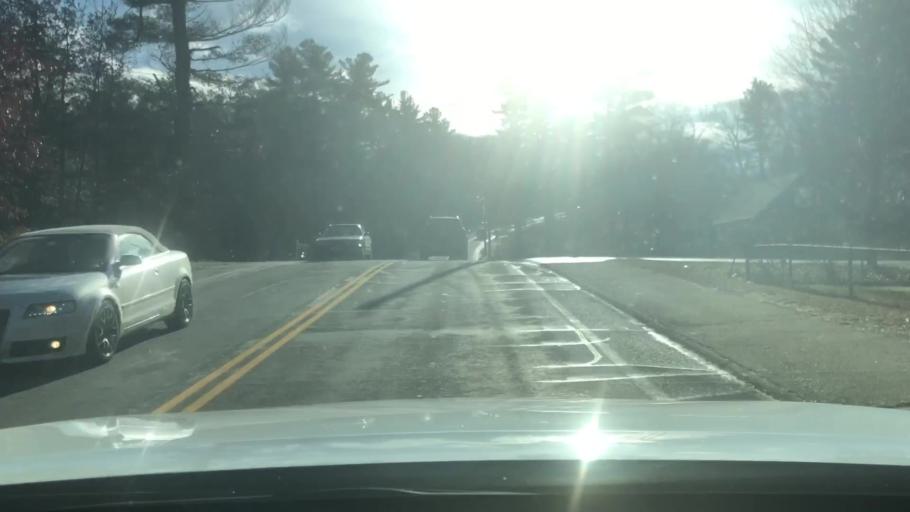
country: US
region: Rhode Island
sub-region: Providence County
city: Woonsocket
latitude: 42.0222
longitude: -71.4864
